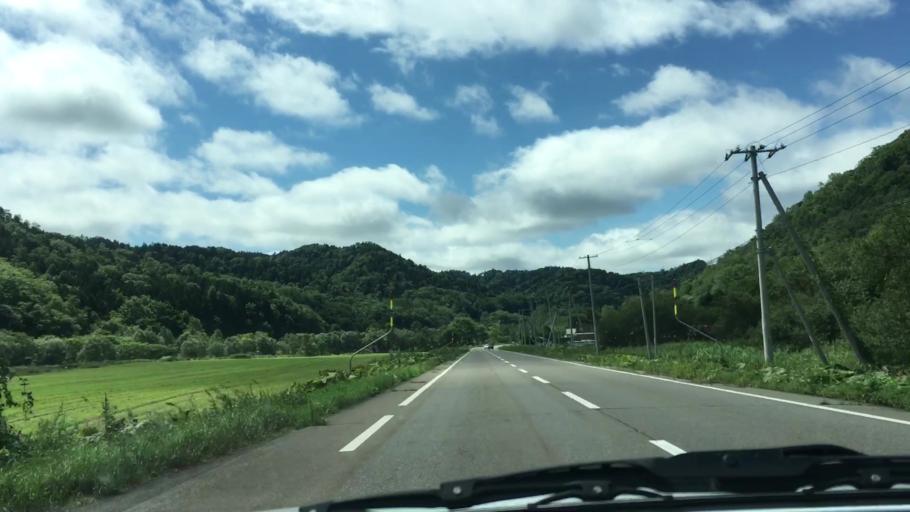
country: JP
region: Hokkaido
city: Kitami
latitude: 43.3644
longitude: 143.8566
